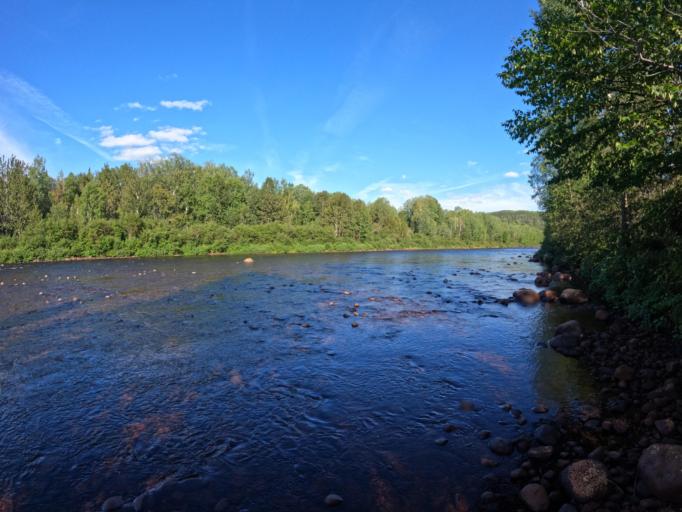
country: CA
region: Quebec
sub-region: Capitale-Nationale
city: Baie-Saint-Paul
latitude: 47.9237
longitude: -70.7136
